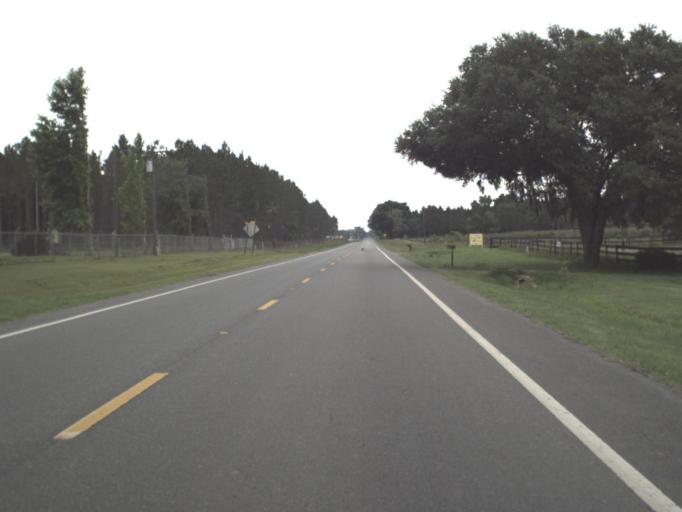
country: US
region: Florida
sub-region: Levy County
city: Williston
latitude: 29.3629
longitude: -82.4558
